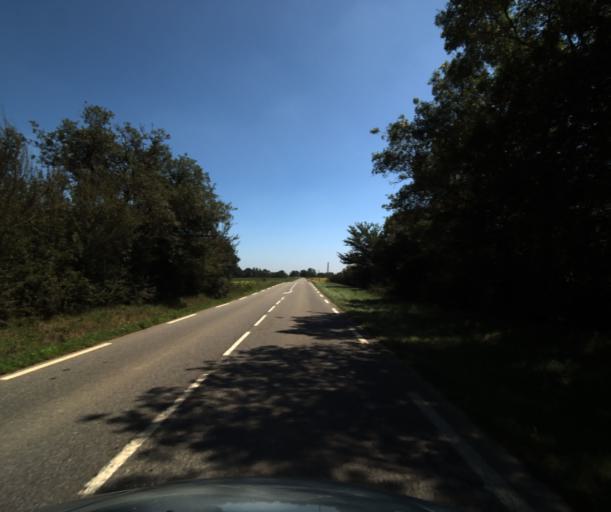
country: FR
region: Midi-Pyrenees
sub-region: Departement de la Haute-Garonne
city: Fonsorbes
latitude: 43.5075
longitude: 1.2363
